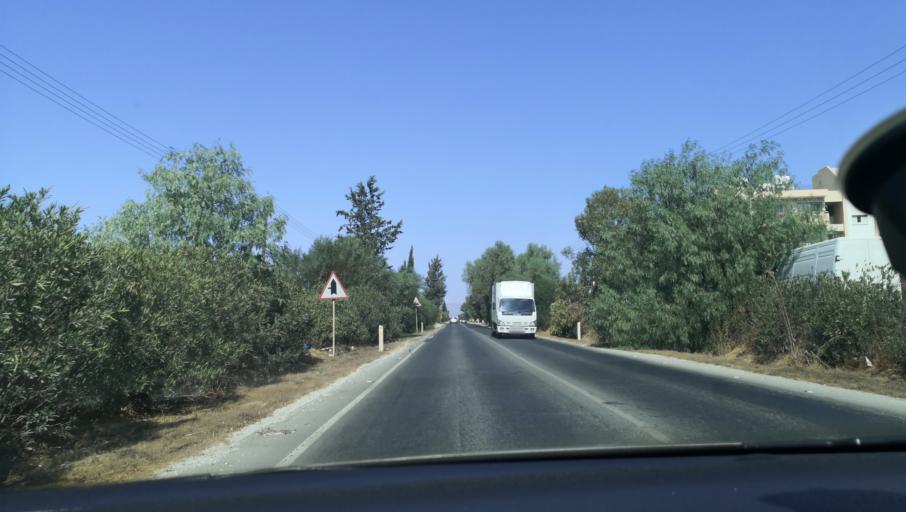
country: CY
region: Lefkosia
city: Kato Deftera
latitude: 35.1017
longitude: 33.2867
